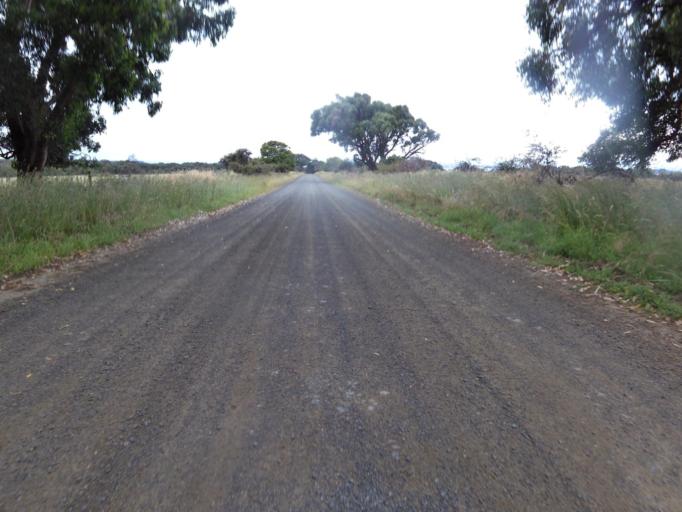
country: AU
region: Victoria
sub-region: Bass Coast
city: Cowes
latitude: -38.3822
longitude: 145.3823
